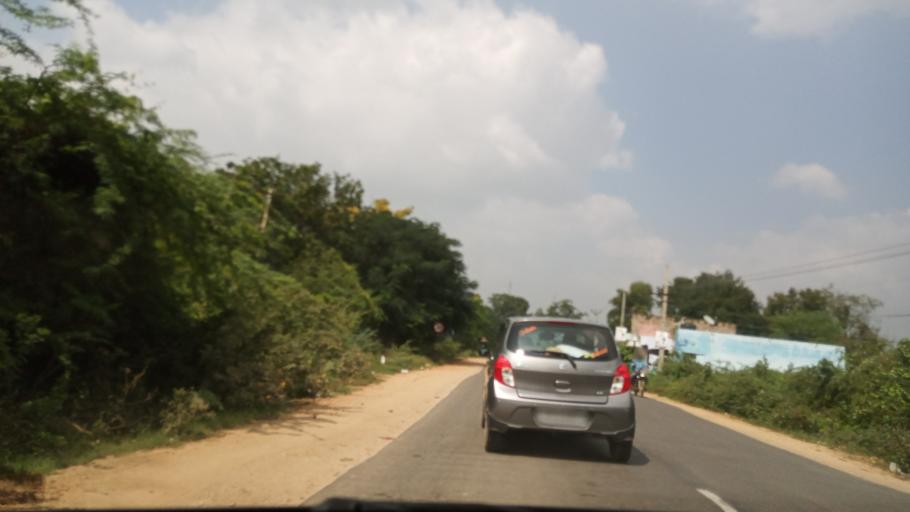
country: IN
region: Andhra Pradesh
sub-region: Chittoor
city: Madanapalle
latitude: 13.6346
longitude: 78.5548
